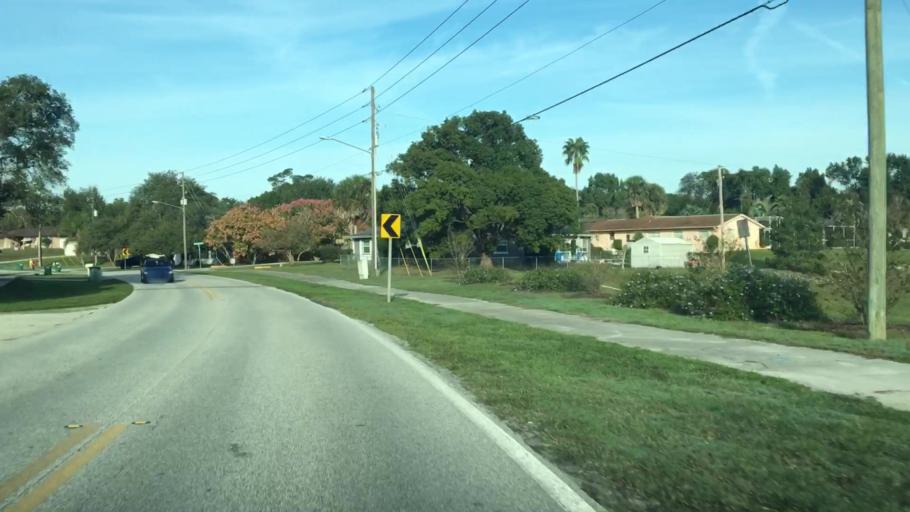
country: US
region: Florida
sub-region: Volusia County
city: Deltona
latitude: 28.9182
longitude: -81.2317
